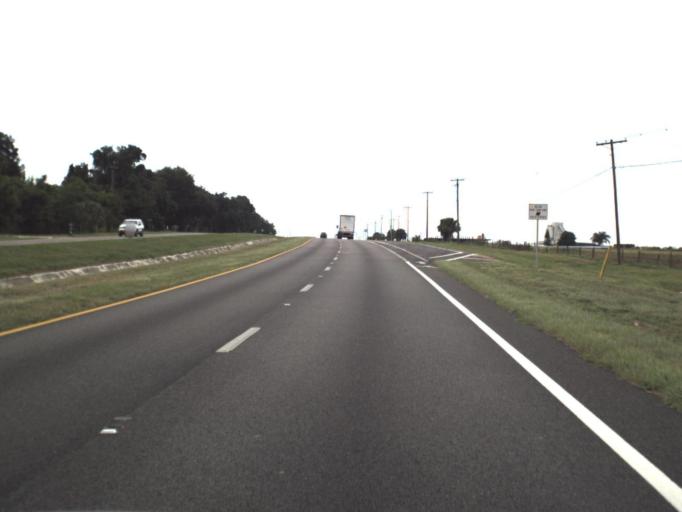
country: US
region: Florida
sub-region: Polk County
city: Bartow
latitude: 27.8584
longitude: -81.8284
